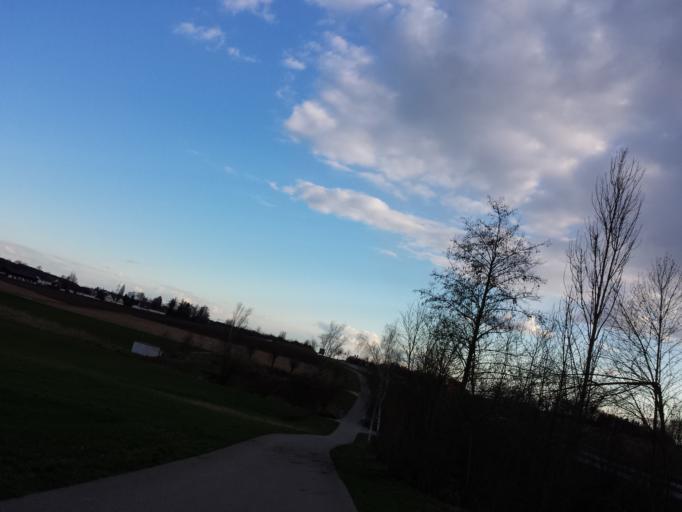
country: DE
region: Bavaria
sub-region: Swabia
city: Guenzburg
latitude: 48.4427
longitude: 10.2894
